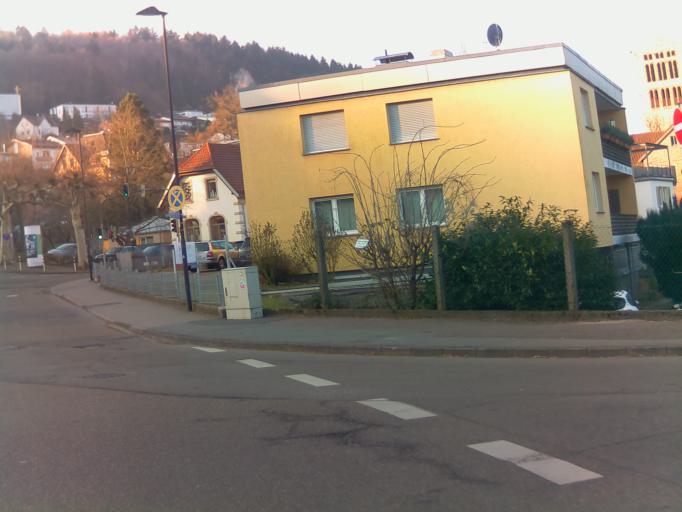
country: DE
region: Baden-Wuerttemberg
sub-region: Karlsruhe Region
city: Mosbach
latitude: 49.3513
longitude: 9.1482
